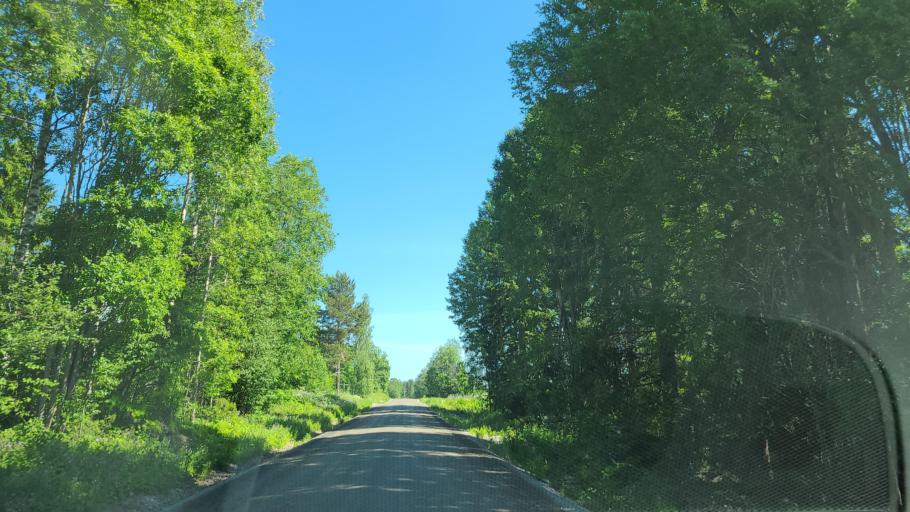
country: SE
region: Vaesterbotten
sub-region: Bjurholms Kommun
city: Bjurholm
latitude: 63.6781
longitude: 19.0053
